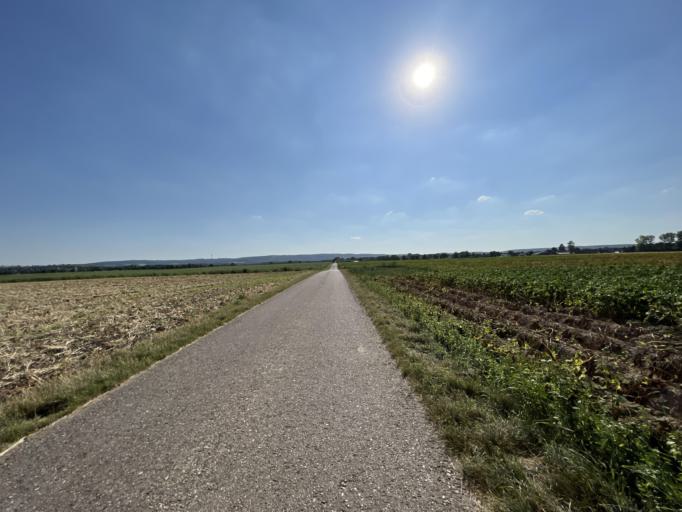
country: DE
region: North Rhine-Westphalia
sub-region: Regierungsbezirk Koln
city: Dueren
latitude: 50.7879
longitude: 6.4513
